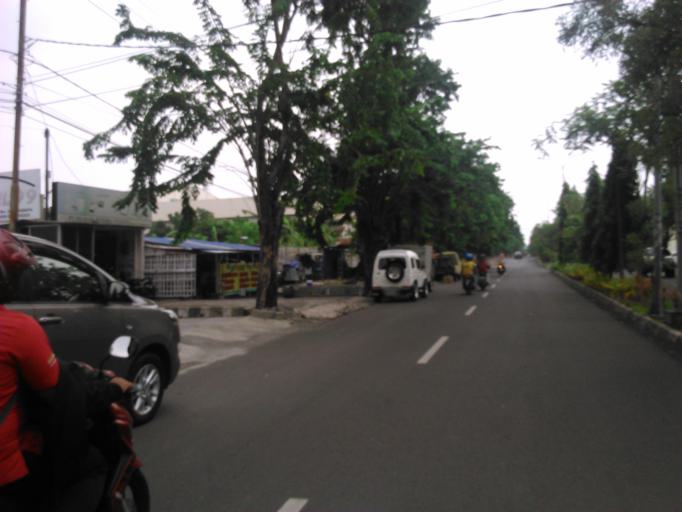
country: ID
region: East Java
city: Gubengairlangga
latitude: -7.2782
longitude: 112.7623
